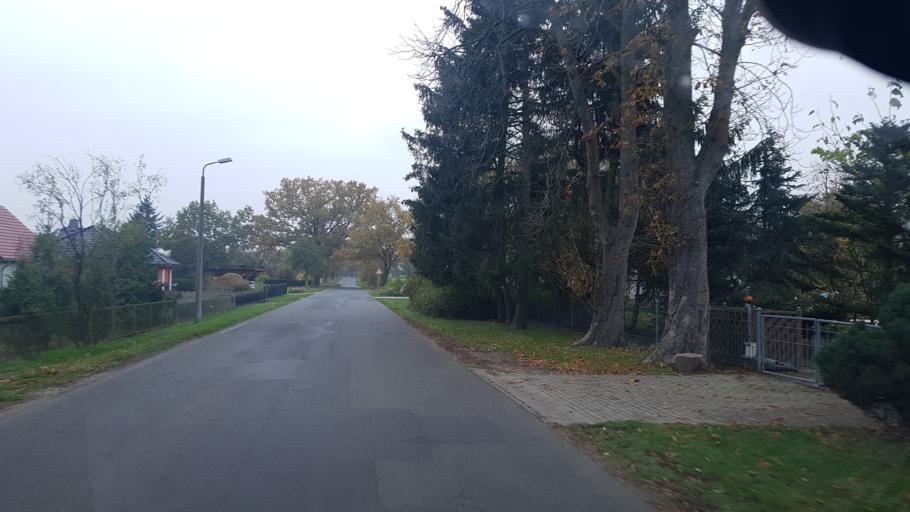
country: DE
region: Brandenburg
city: Schonermark
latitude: 52.9189
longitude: 13.1251
